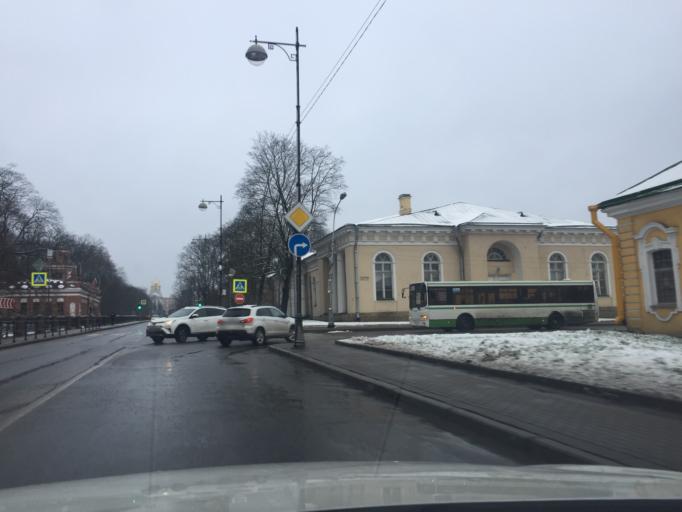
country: RU
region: St.-Petersburg
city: Pushkin
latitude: 59.7141
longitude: 30.4069
